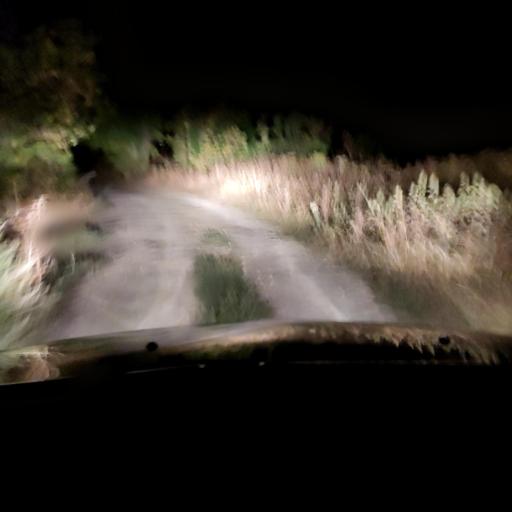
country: RU
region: Voronezj
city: Semiluki
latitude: 51.7204
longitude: 38.9950
